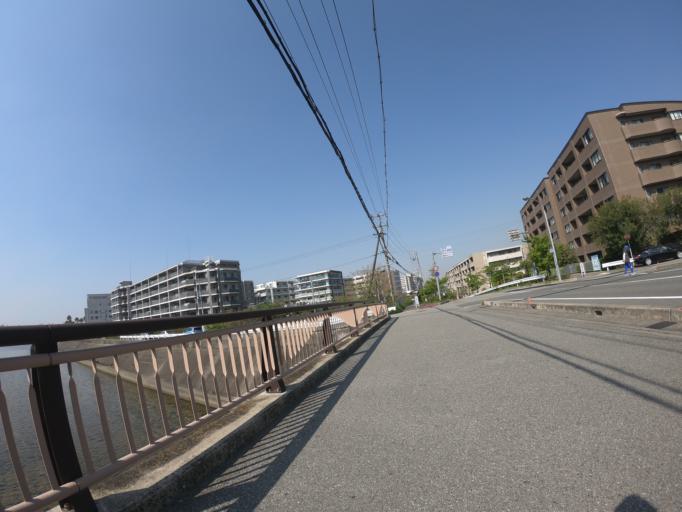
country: JP
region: Hyogo
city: Nishinomiya-hama
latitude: 34.7272
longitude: 135.3290
